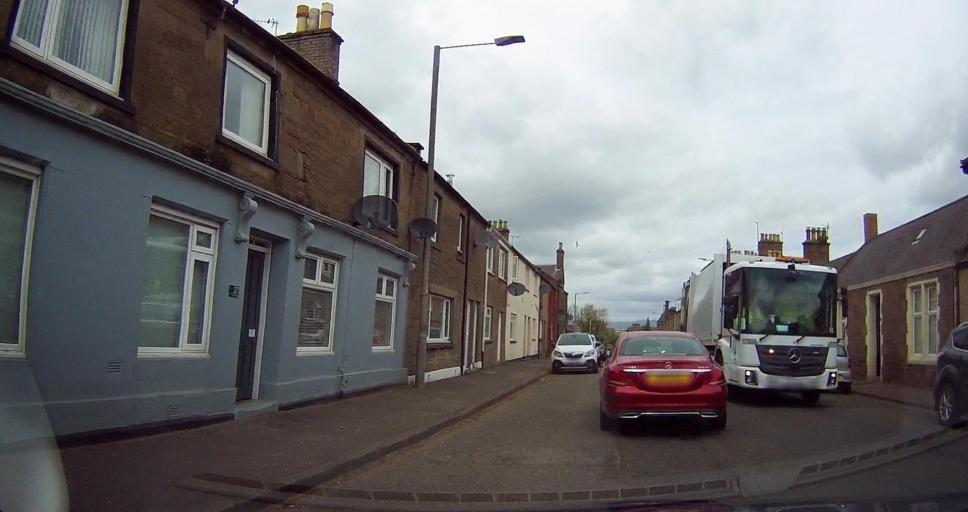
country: GB
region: Scotland
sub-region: Angus
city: Forfar
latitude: 56.6469
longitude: -2.8817
